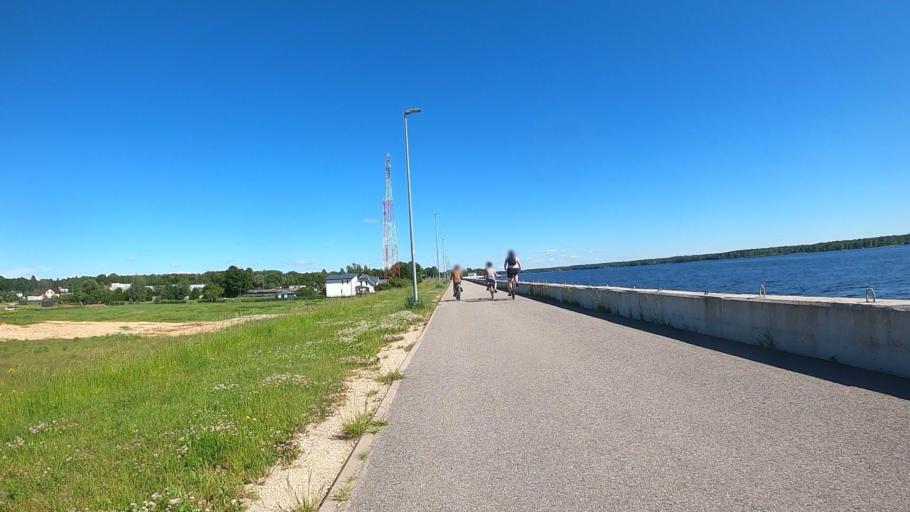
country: LV
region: Ikskile
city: Ikskile
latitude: 56.8320
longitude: 24.4780
